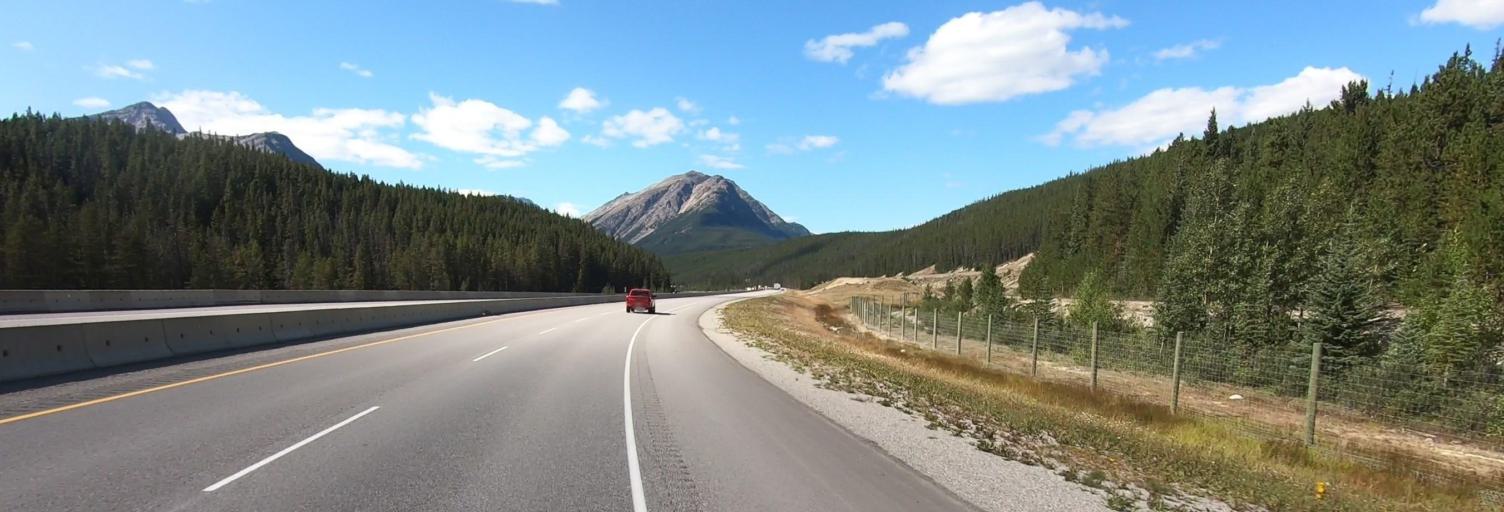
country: CA
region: Alberta
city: Lake Louise
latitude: 51.4459
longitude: -116.2501
